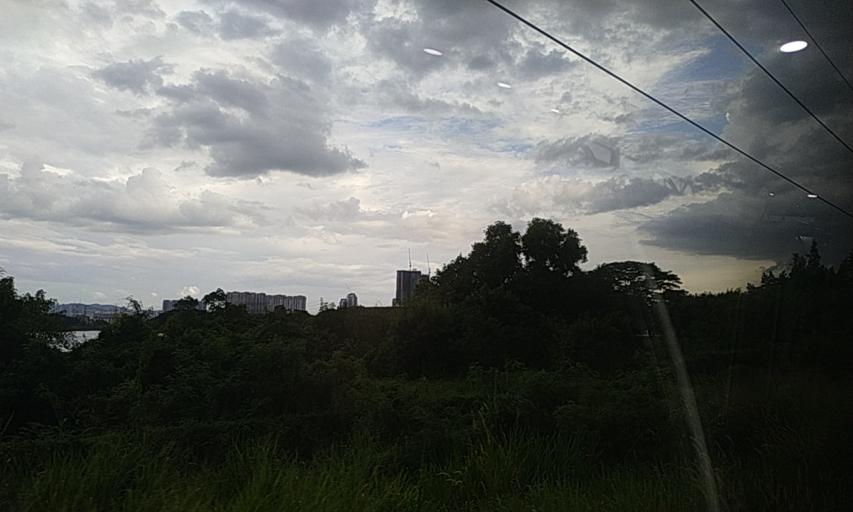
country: MY
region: Kuala Lumpur
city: Kuala Lumpur
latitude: 3.2210
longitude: 101.6725
